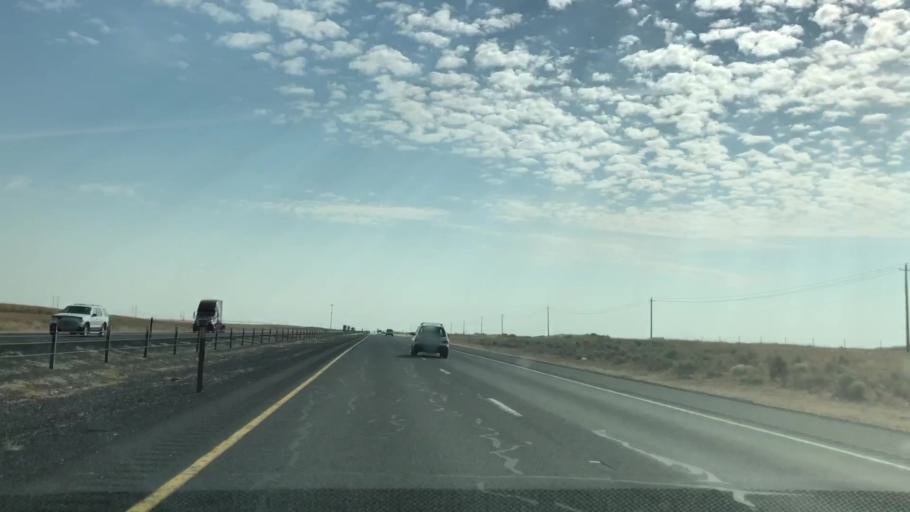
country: US
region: Washington
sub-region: Grant County
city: Cascade Valley
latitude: 47.1042
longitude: -119.5122
